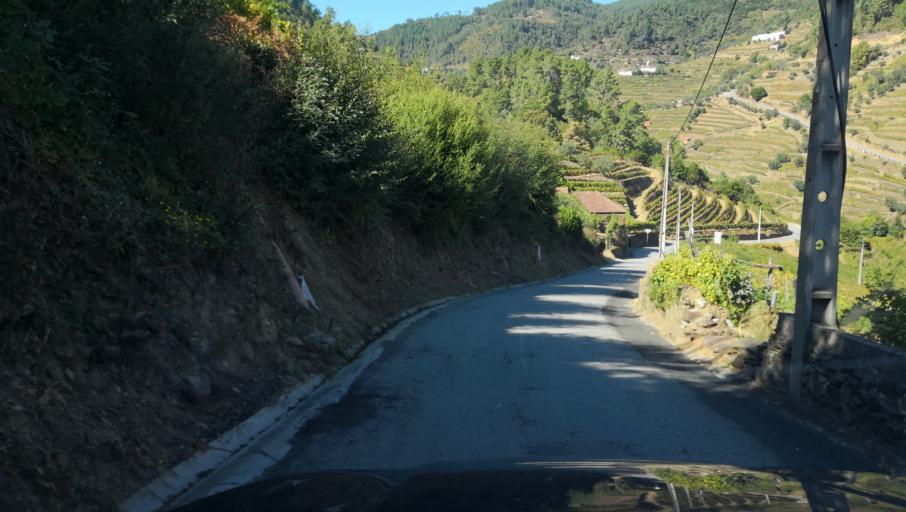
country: PT
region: Vila Real
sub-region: Santa Marta de Penaguiao
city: Santa Marta de Penaguiao
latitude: 41.2479
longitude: -7.8130
